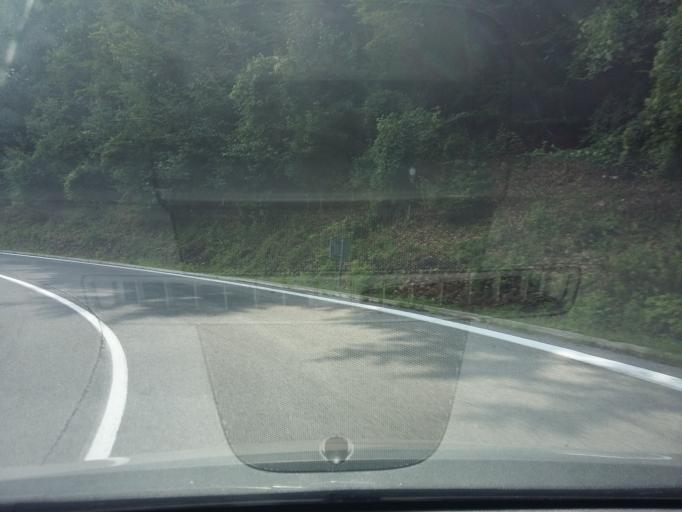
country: SK
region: Bratislavsky
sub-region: Okres Pezinok
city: Pezinok
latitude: 48.3514
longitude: 17.2117
